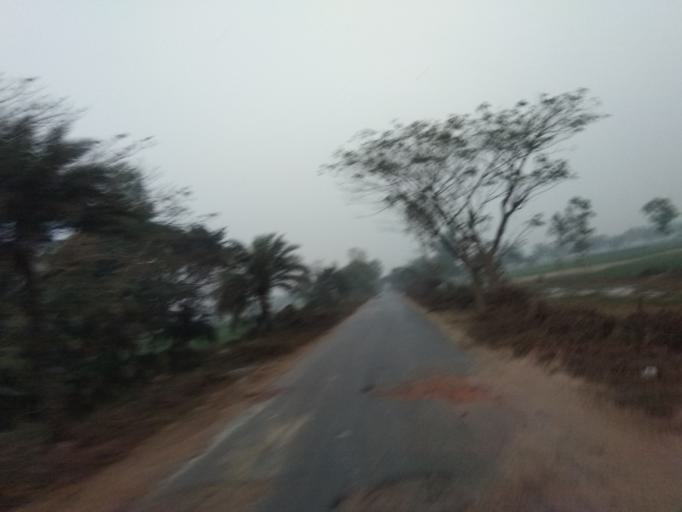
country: BD
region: Rajshahi
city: Bogra
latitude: 24.7440
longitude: 89.3363
